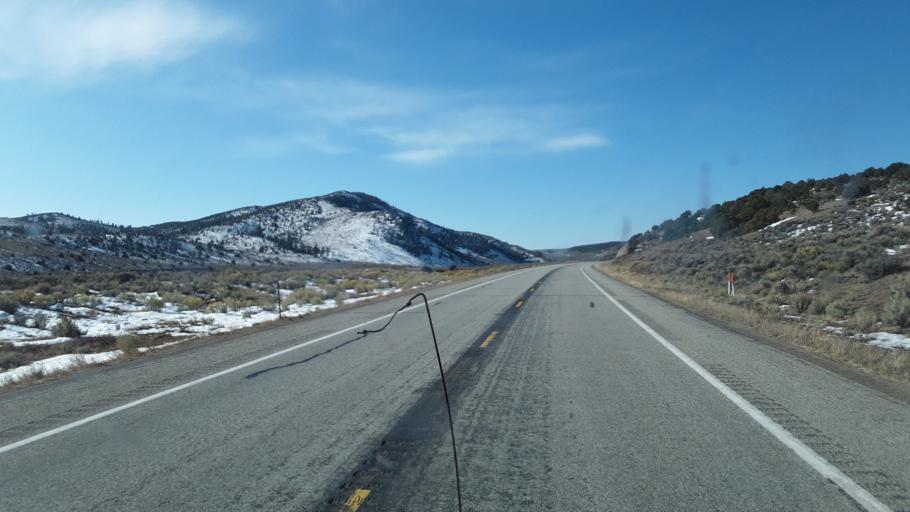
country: US
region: Colorado
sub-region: Costilla County
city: San Luis
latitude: 37.5083
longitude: -105.3183
